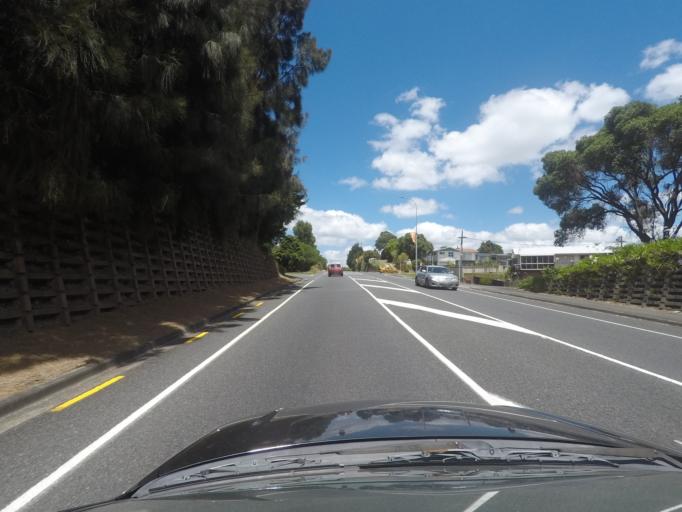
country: NZ
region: Northland
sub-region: Whangarei
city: Whangarei
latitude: -35.7439
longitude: 174.3662
